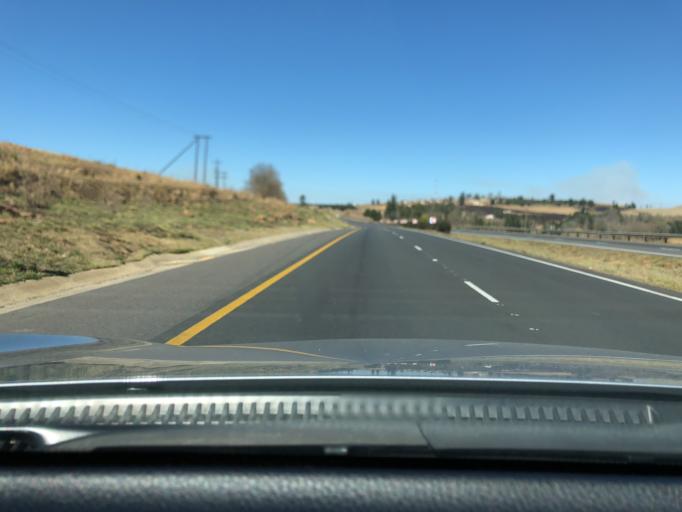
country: ZA
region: KwaZulu-Natal
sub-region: uMgungundlovu District Municipality
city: Mooirivier
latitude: -29.2556
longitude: 30.0203
